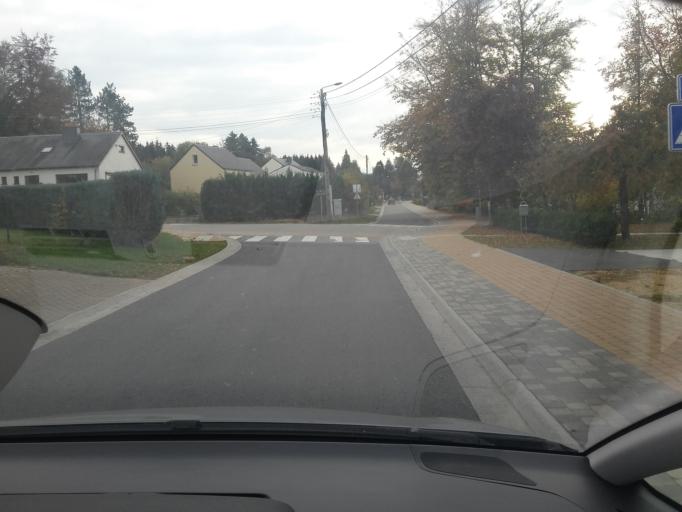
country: BE
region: Wallonia
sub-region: Province du Luxembourg
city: Arlon
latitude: 49.7015
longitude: 5.8193
